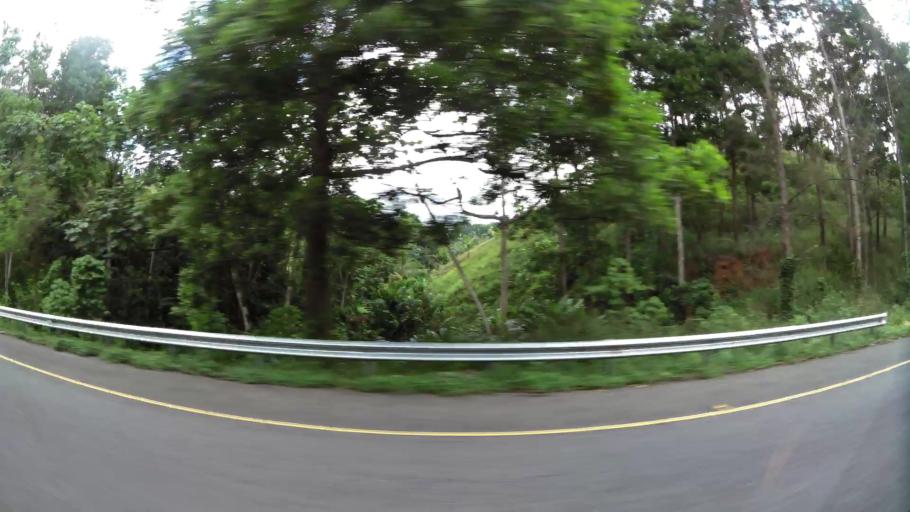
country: DO
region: Monsenor Nouel
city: Piedra Blanca
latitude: 18.8197
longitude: -70.2882
